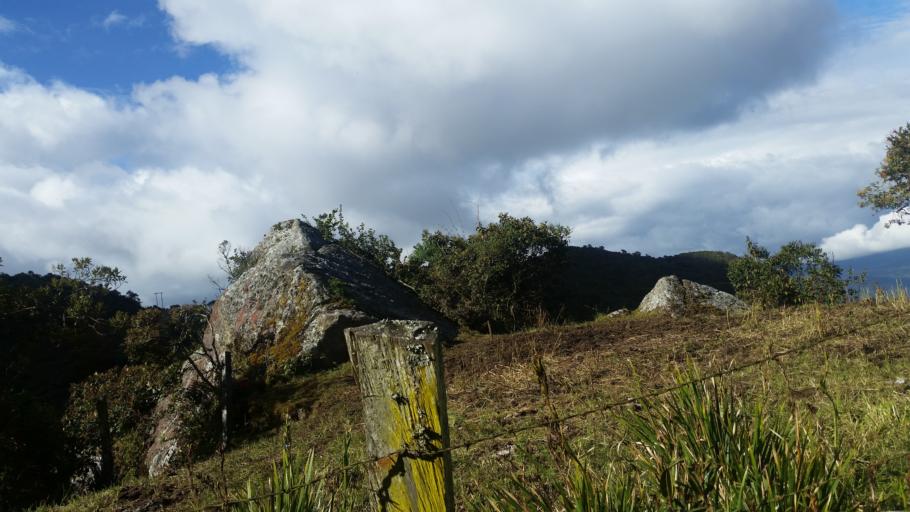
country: CO
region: Cundinamarca
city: Choachi
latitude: 4.5565
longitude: -73.9721
